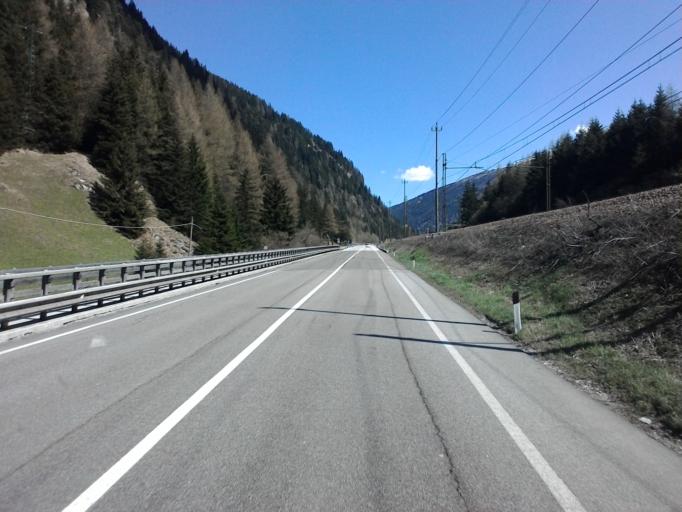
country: IT
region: Trentino-Alto Adige
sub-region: Bolzano
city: Ried
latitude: 46.9862
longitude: 11.4950
